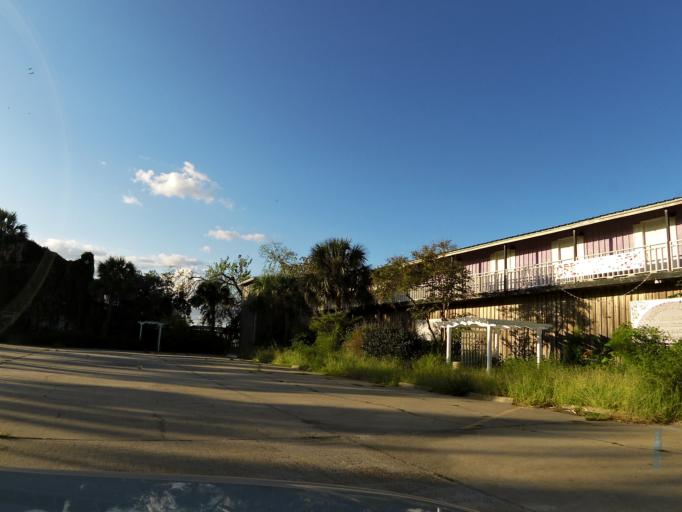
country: US
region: Florida
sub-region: Franklin County
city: Apalachicola
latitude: 29.7268
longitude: -84.9817
